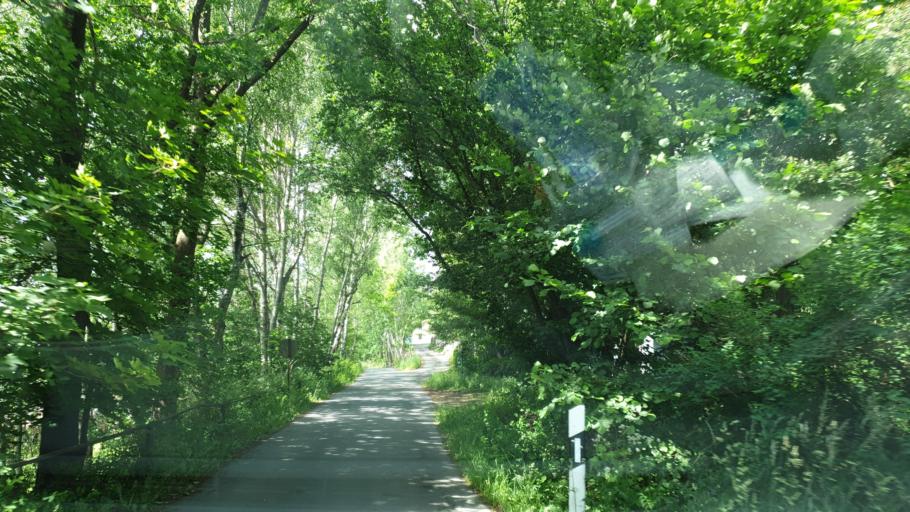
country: DE
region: Saxony
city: Adorf
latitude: 50.3314
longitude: 12.2586
